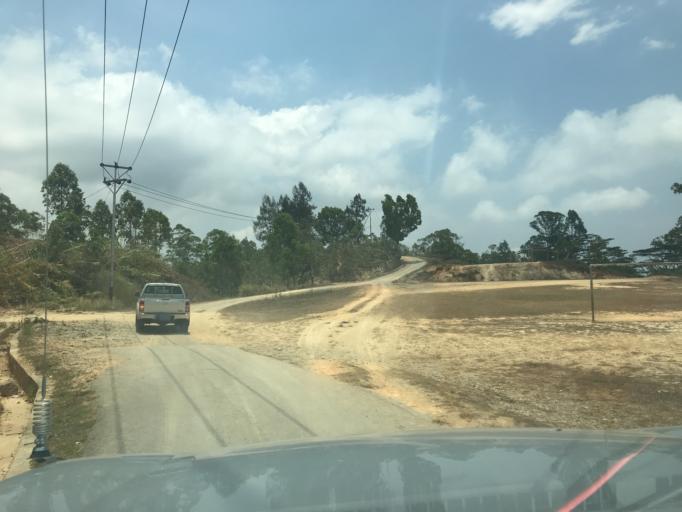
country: TL
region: Dili
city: Dili
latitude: -8.6074
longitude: 125.5875
